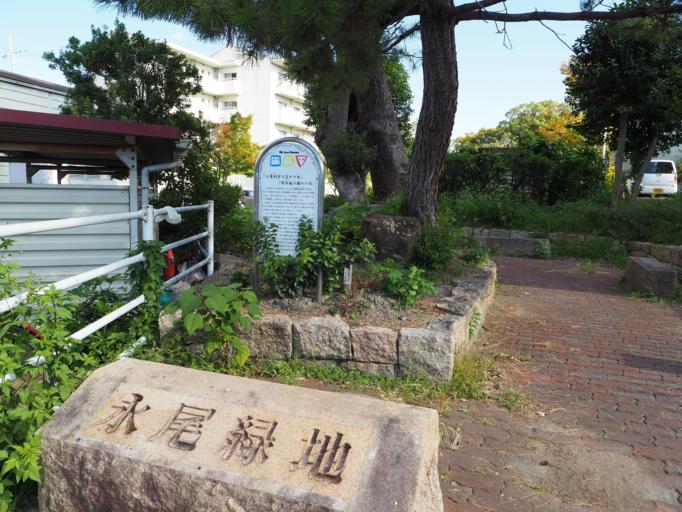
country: JP
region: Osaka
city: Takaishi
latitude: 34.5018
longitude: 135.4399
